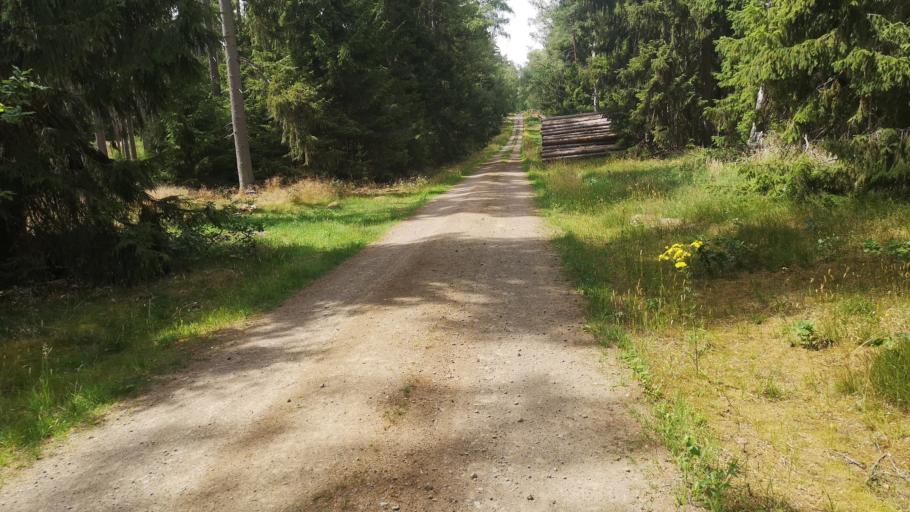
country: DE
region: Lower Saxony
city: Thomasburg
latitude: 53.2365
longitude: 10.7162
